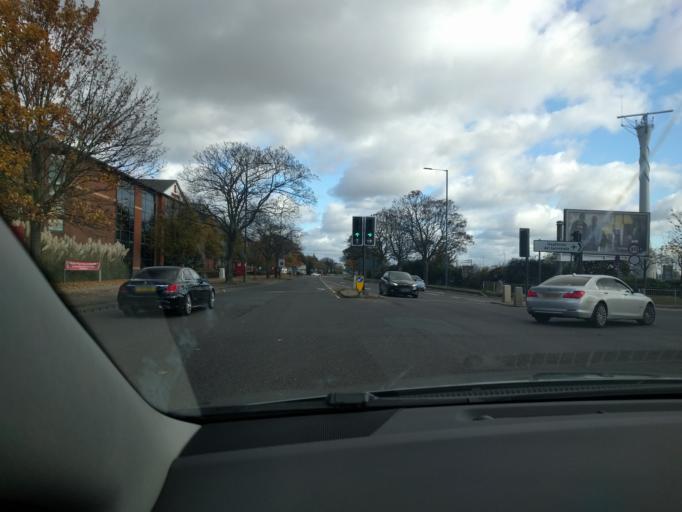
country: GB
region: England
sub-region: Greater London
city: West Drayton
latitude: 51.4811
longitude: -0.4586
